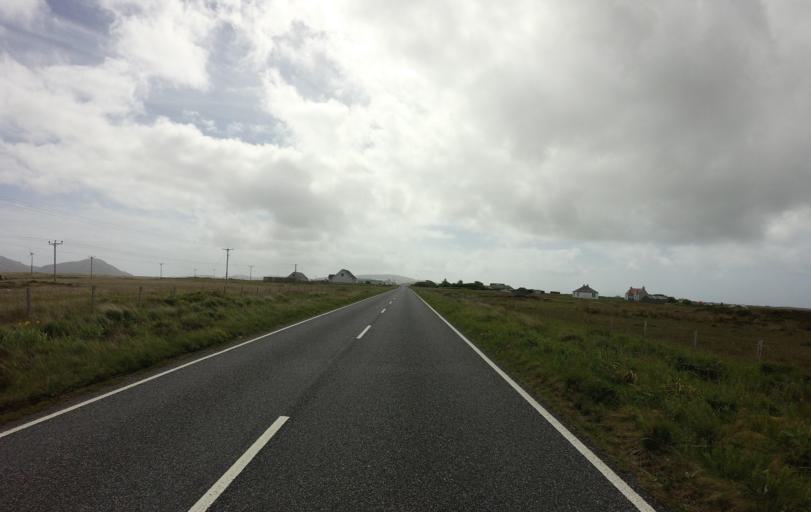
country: GB
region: Scotland
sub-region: Eilean Siar
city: Isle of South Uist
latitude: 57.1762
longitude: -7.3774
